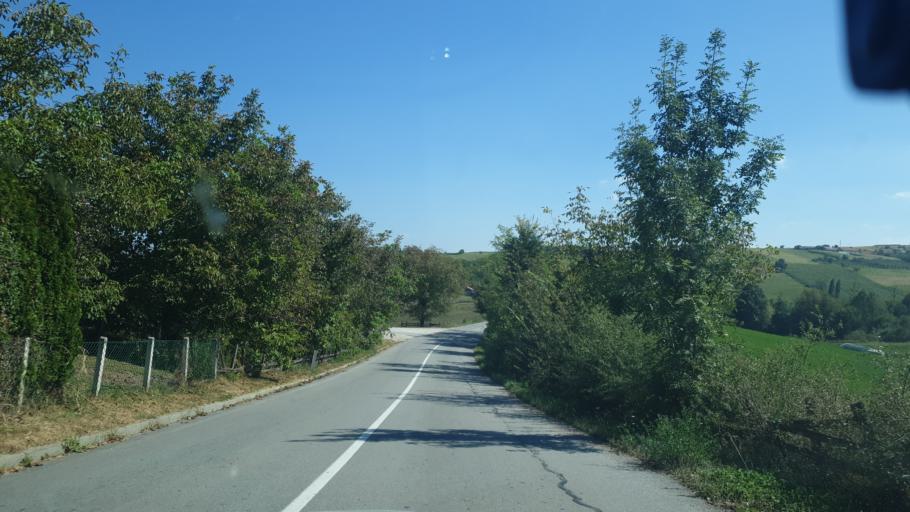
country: RS
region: Central Serbia
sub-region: Kolubarski Okrug
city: Mionica
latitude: 44.1895
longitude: 20.0310
